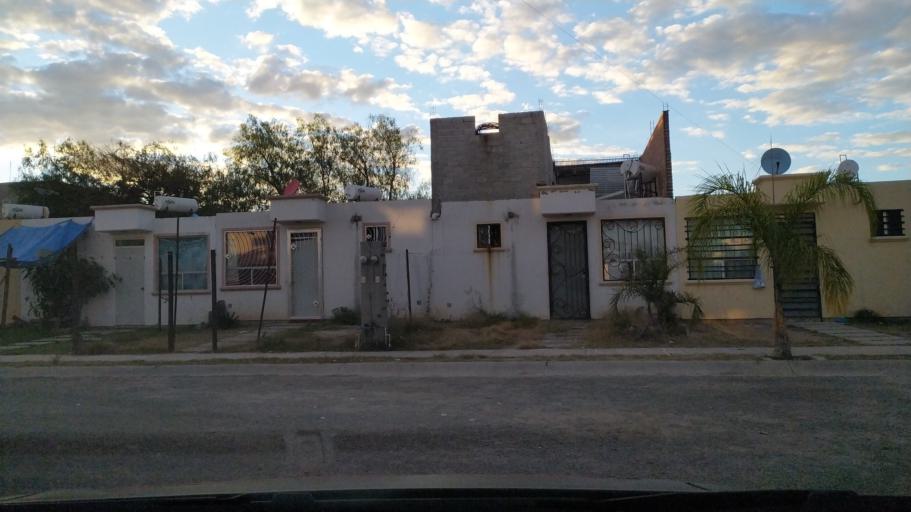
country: MX
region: Guanajuato
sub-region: San Francisco del Rincon
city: Estacion de San Francisco
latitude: 21.0407
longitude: -101.8399
